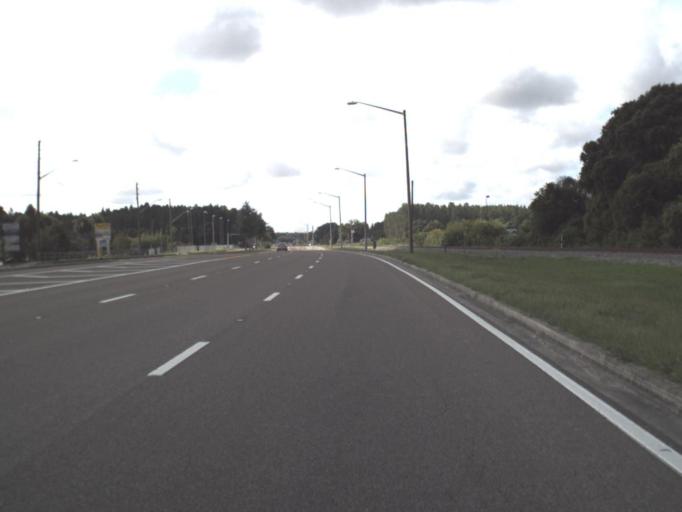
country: US
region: Florida
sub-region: Hillsborough County
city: Lutz
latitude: 28.1813
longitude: -82.4659
